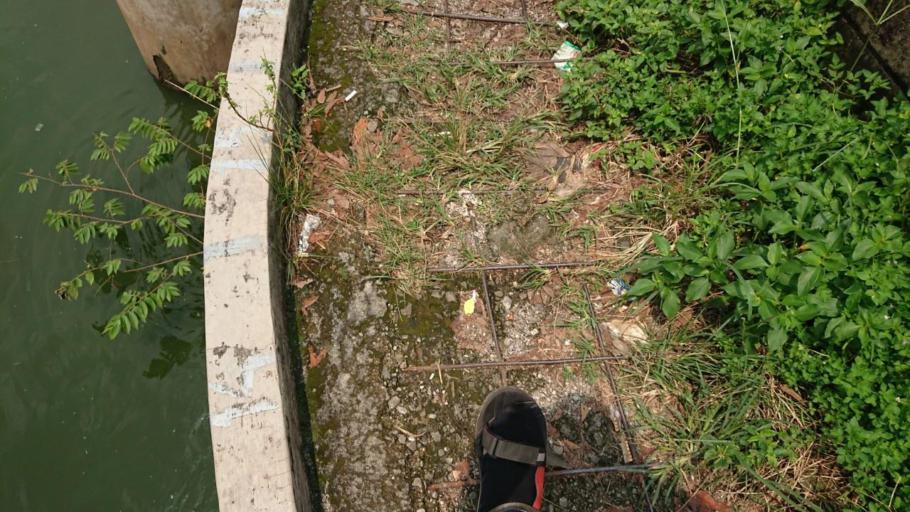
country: ID
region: West Java
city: Depok
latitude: -6.3534
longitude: 106.8682
